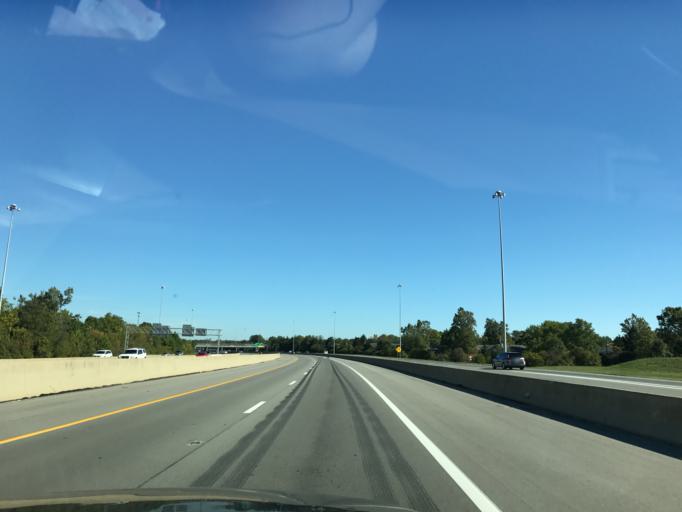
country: US
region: Ohio
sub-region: Franklin County
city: Blacklick Estates
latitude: 39.9371
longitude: -82.8491
